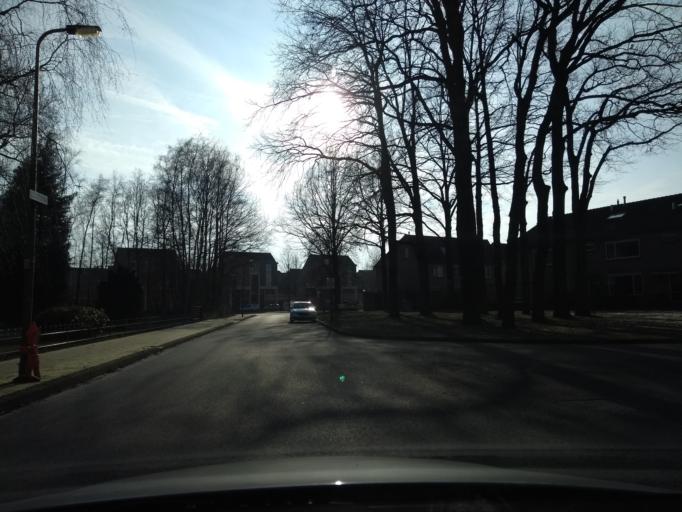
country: NL
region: Overijssel
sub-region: Gemeente Hengelo
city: Hengelo
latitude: 52.2675
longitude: 6.8312
